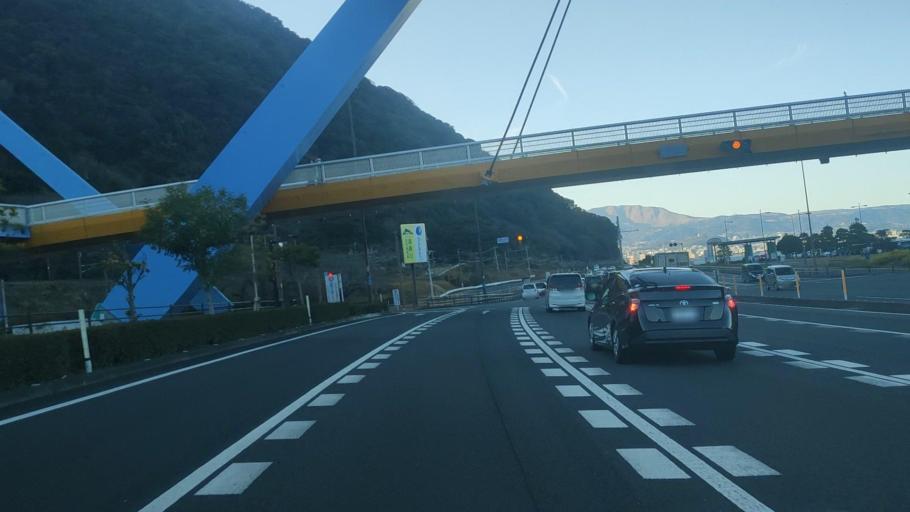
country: JP
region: Oita
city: Beppu
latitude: 33.2583
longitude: 131.5345
